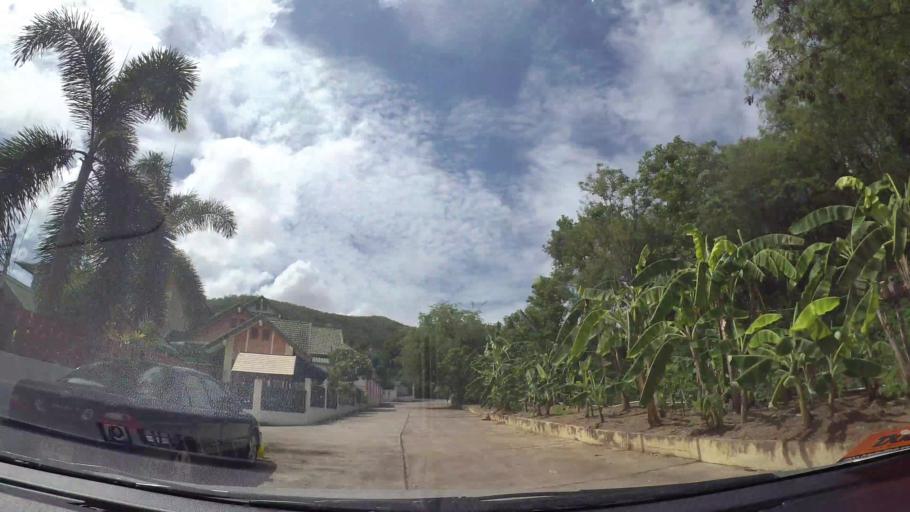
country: TH
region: Chon Buri
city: Sattahip
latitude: 12.6954
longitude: 100.9115
